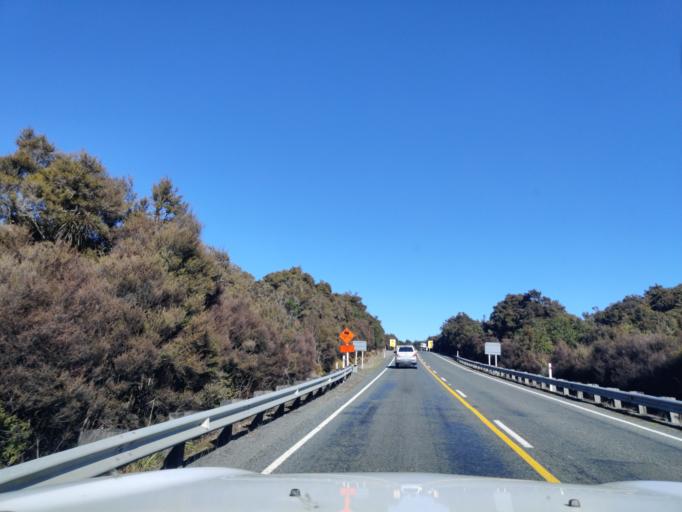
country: NZ
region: Waikato
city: Turangi
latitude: -39.1482
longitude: 175.7694
